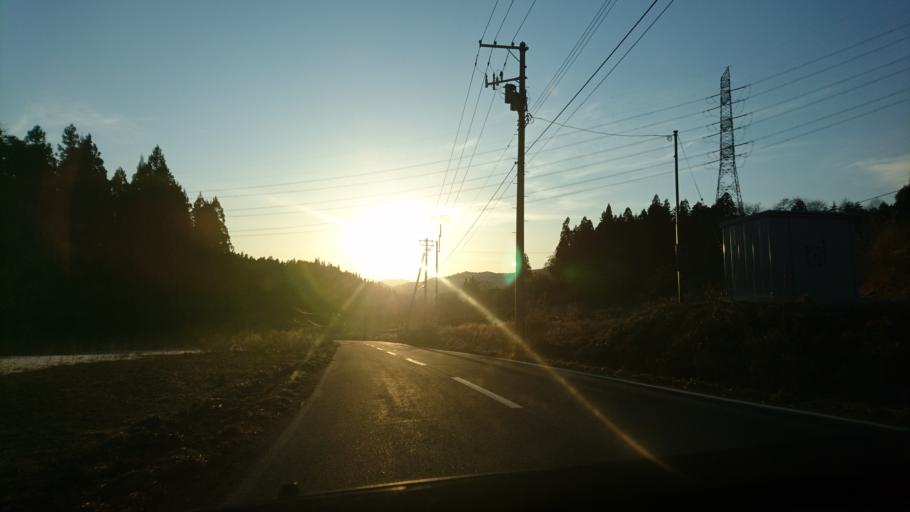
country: JP
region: Iwate
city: Mizusawa
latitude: 39.0408
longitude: 141.3126
